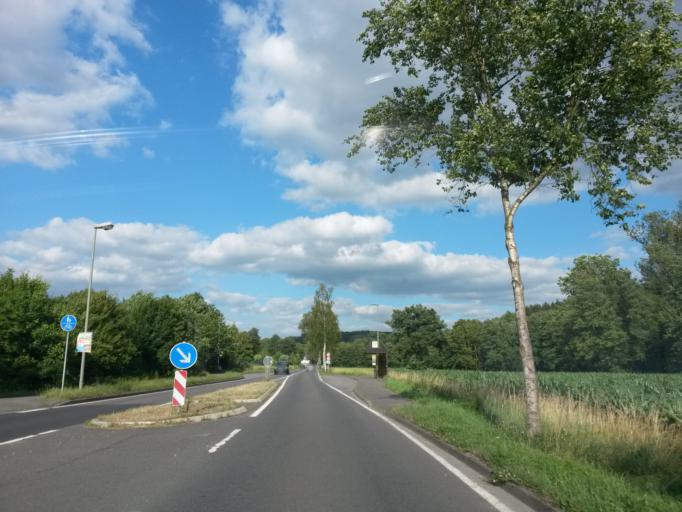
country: DE
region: North Rhine-Westphalia
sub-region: Regierungsbezirk Koln
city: Ruppichteroth
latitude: 50.8462
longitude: 7.4929
